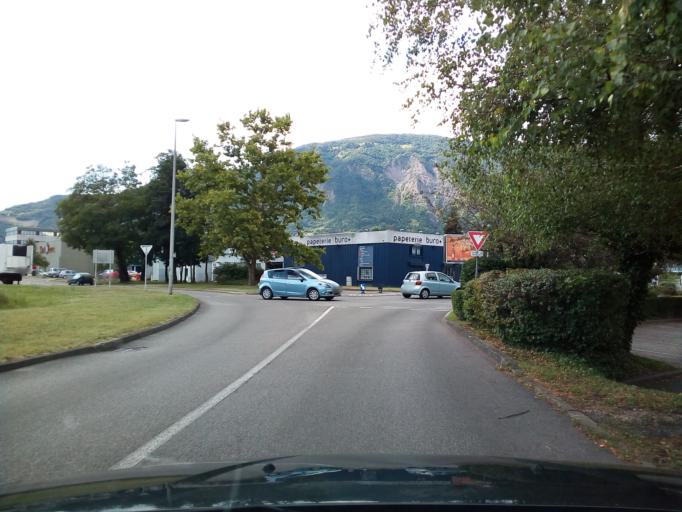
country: FR
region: Rhone-Alpes
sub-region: Departement de l'Isere
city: Corenc
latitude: 45.2027
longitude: 5.7686
